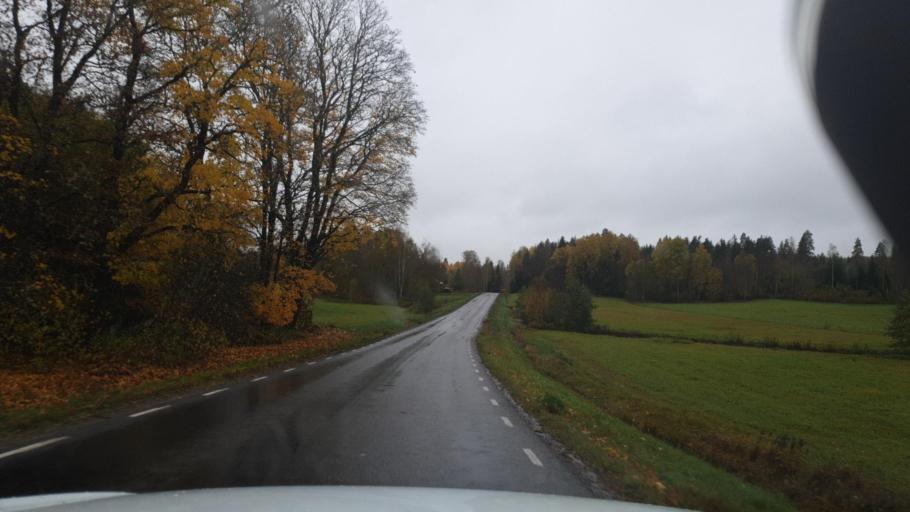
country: SE
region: Vaermland
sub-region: Eda Kommun
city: Charlottenberg
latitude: 59.8048
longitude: 12.1522
